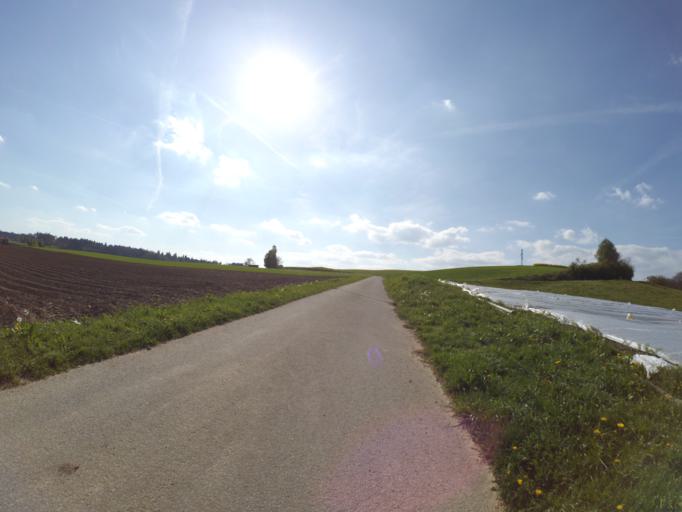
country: CH
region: Thurgau
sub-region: Frauenfeld District
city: Diessenhofen
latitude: 47.6606
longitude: 8.7676
